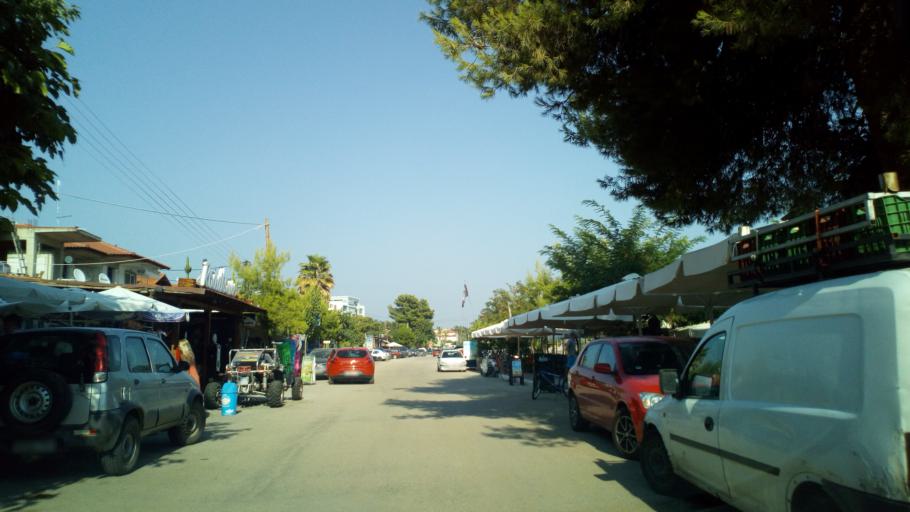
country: GR
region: Central Macedonia
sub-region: Nomos Chalkidikis
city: Ormylia
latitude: 40.2595
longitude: 23.4934
